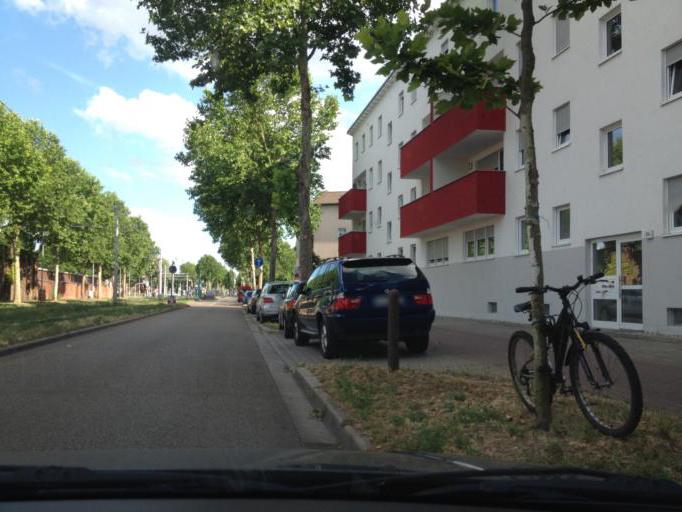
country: DE
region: Baden-Wuerttemberg
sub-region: Karlsruhe Region
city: Mannheim
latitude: 49.4667
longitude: 8.4737
